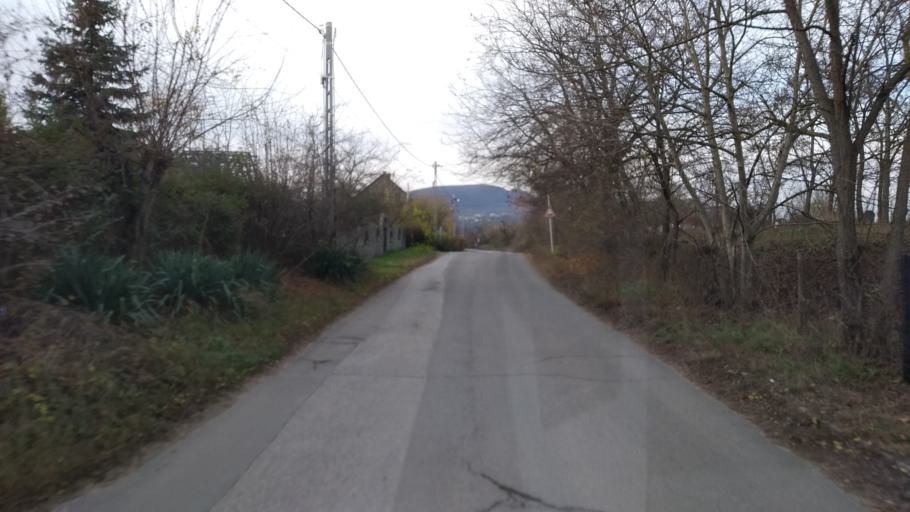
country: HU
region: Pest
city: God
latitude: 47.6880
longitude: 19.1099
